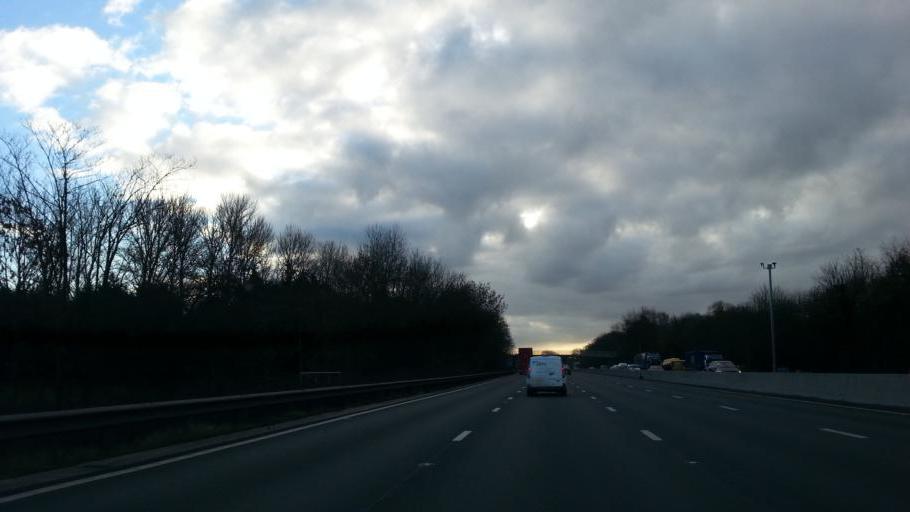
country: GB
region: England
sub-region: Northamptonshire
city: Long Buckby
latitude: 52.2612
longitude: -1.0866
